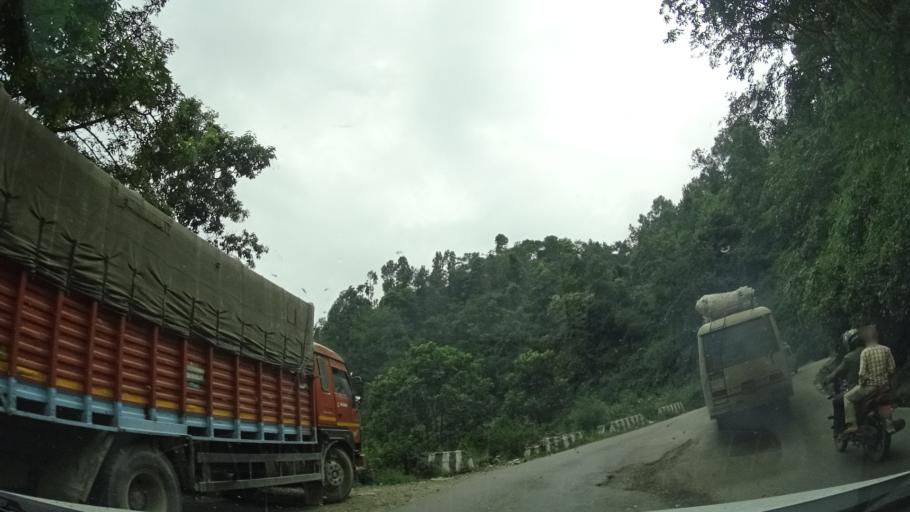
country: NP
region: Central Region
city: Kirtipur
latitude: 27.7122
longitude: 85.2005
